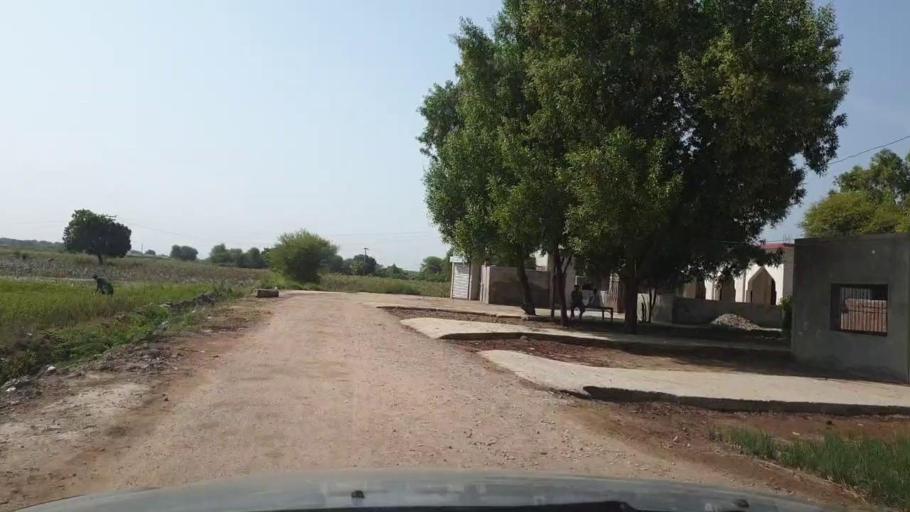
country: PK
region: Sindh
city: Tando Ghulam Ali
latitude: 25.1332
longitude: 68.8720
